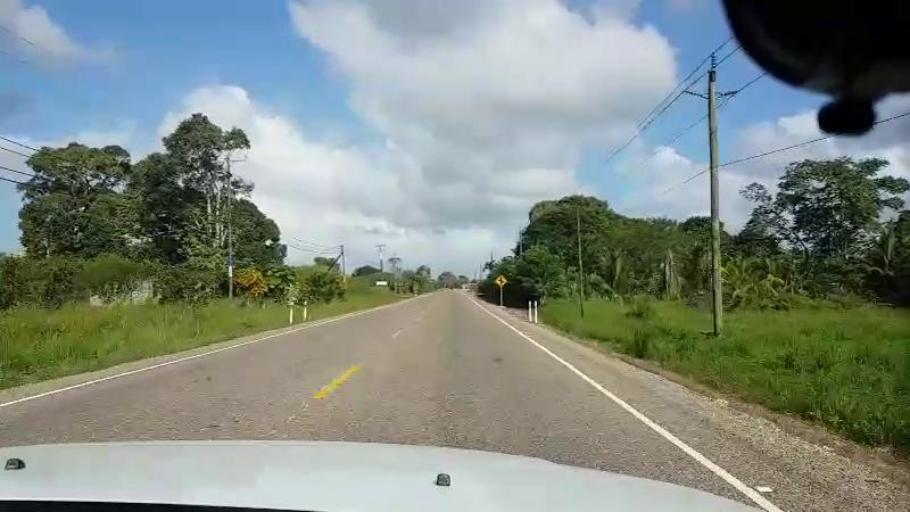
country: BZ
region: Stann Creek
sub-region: Dangriga
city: Dangriga
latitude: 16.9968
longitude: -88.3537
